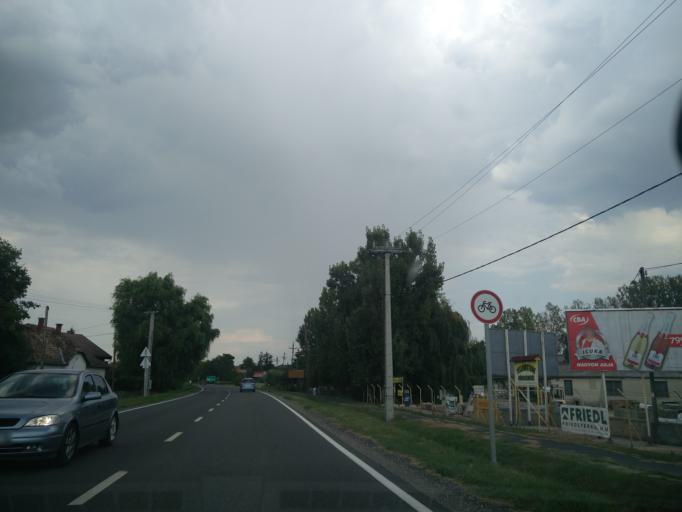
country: HU
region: Fejer
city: Polgardi
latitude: 47.0484
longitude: 18.3016
